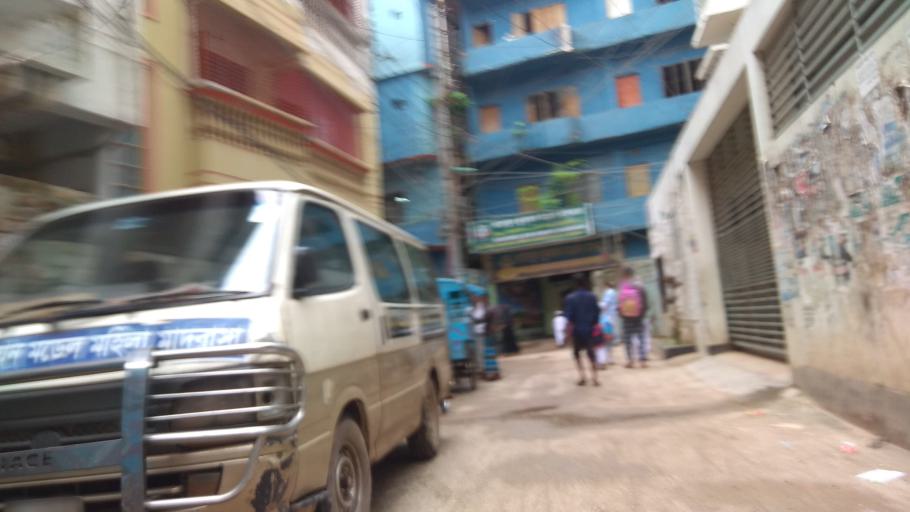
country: BD
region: Dhaka
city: Azimpur
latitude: 23.8002
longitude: 90.3669
